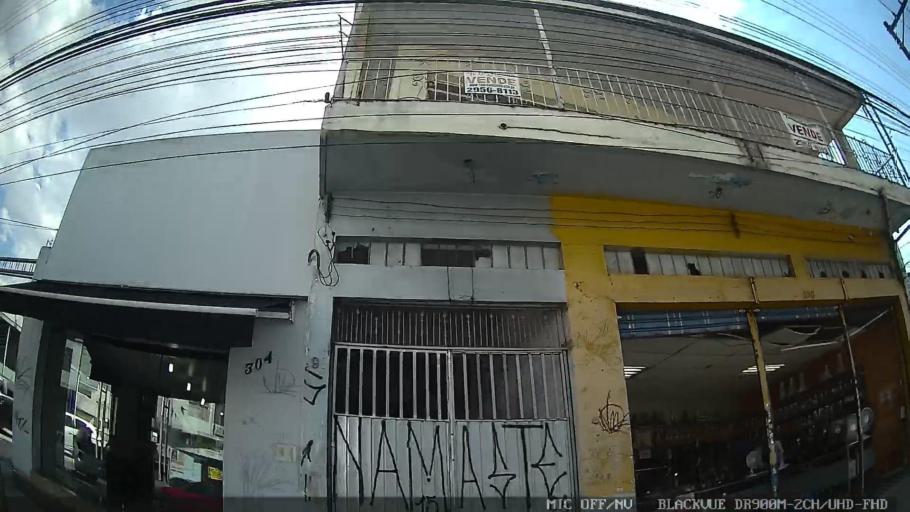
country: BR
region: Sao Paulo
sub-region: Ferraz De Vasconcelos
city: Ferraz de Vasconcelos
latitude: -23.4959
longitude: -46.4424
